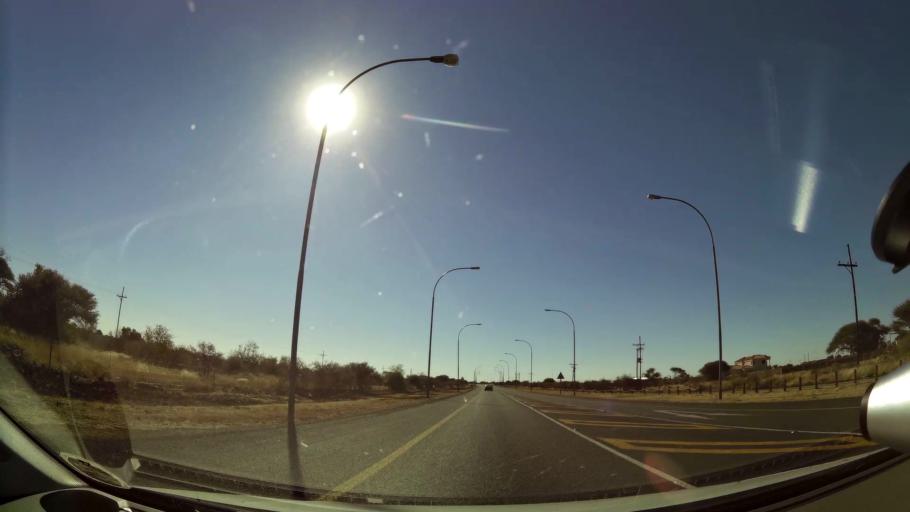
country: ZA
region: Northern Cape
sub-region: Frances Baard District Municipality
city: Warrenton
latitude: -28.1073
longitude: 24.8620
